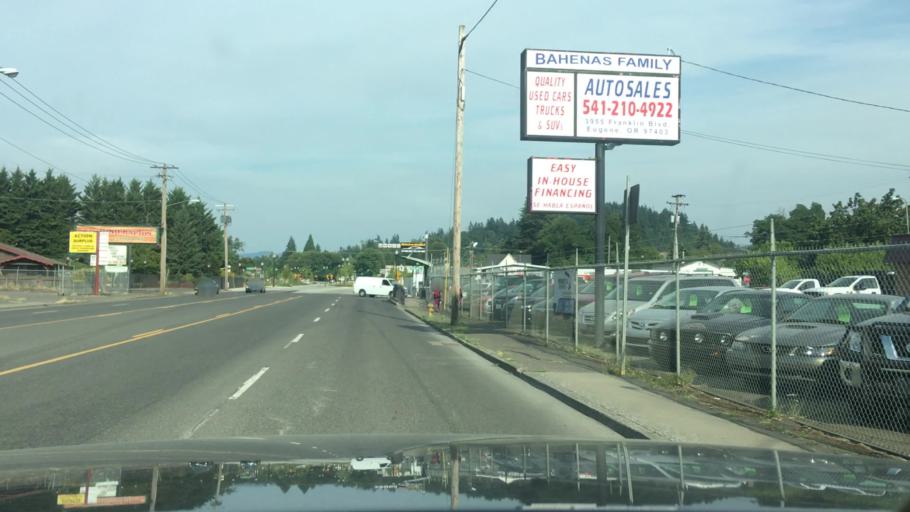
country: US
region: Oregon
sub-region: Lane County
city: Springfield
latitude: 44.0447
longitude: -123.0358
